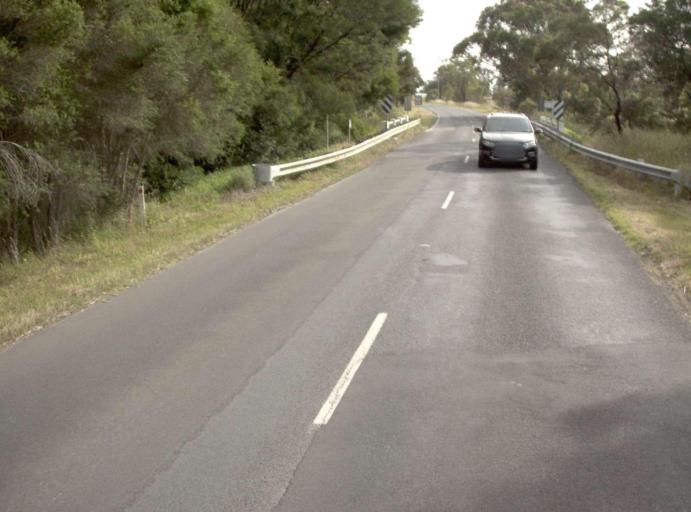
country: AU
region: Victoria
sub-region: Latrobe
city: Traralgon
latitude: -38.0623
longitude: 146.6214
